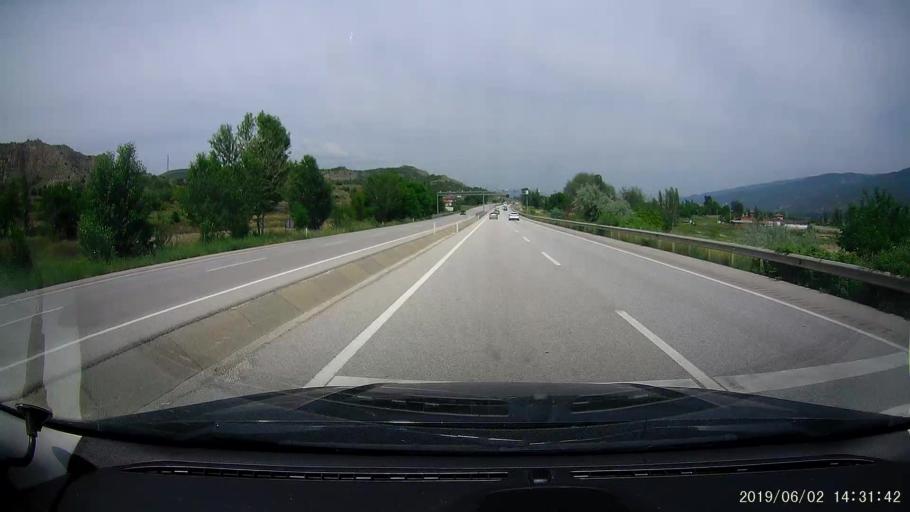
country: TR
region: Kastamonu
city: Tosya
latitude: 41.0212
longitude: 34.1422
